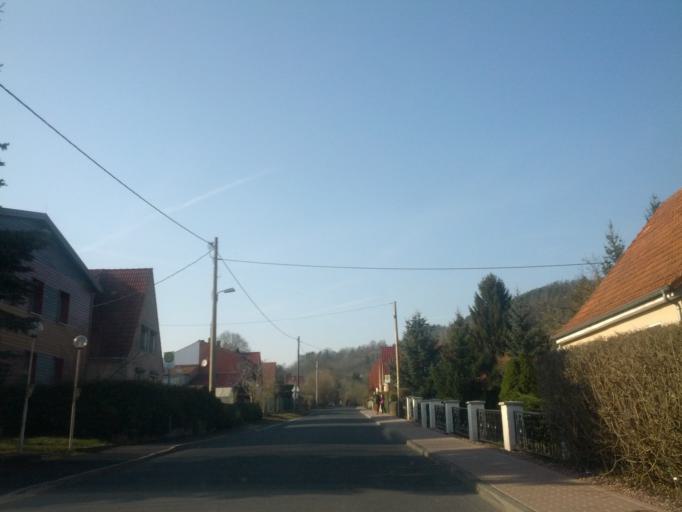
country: DE
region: Thuringia
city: Creuzburg
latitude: 51.0527
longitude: 10.2414
